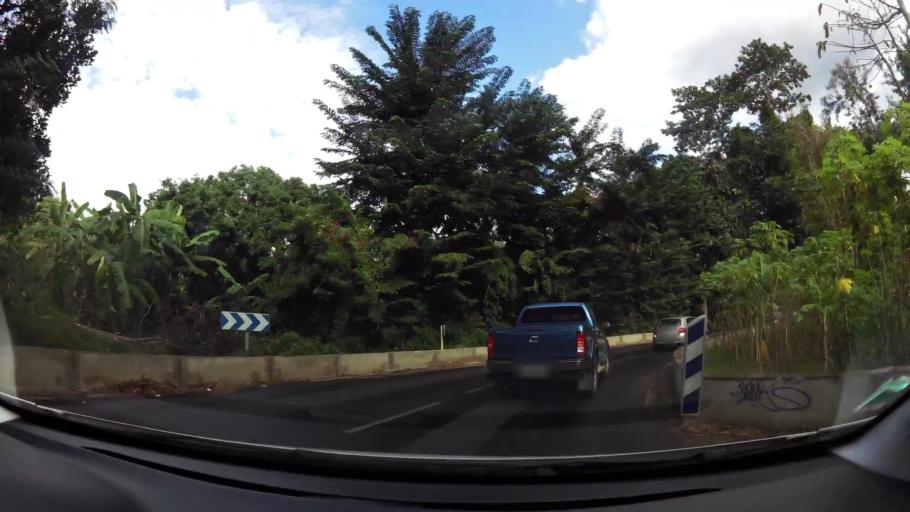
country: YT
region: Ouangani
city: Ouangani
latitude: -12.8372
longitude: 45.1509
